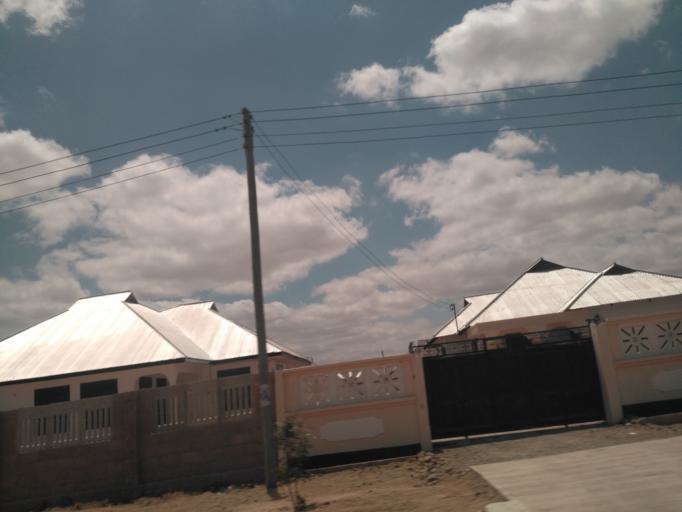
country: TZ
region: Dodoma
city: Kisasa
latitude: -6.1747
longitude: 35.7995
